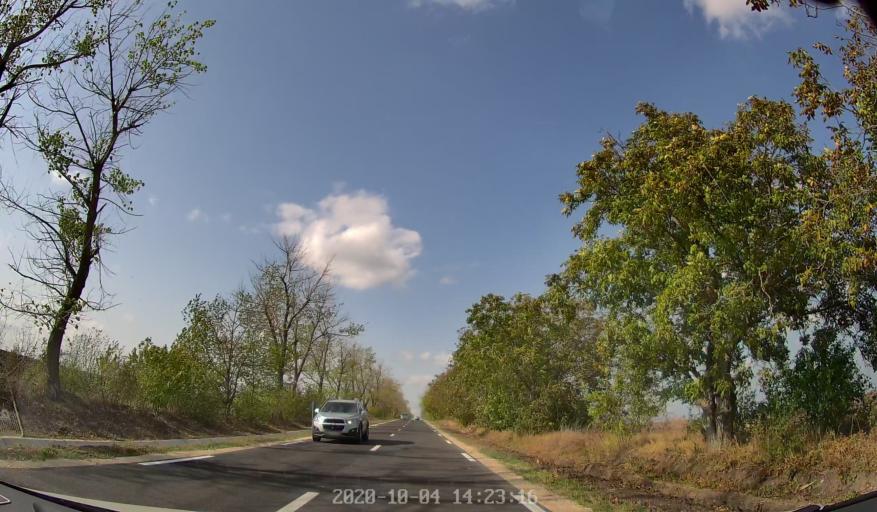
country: MD
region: Rezina
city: Saharna
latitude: 47.6067
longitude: 28.9379
